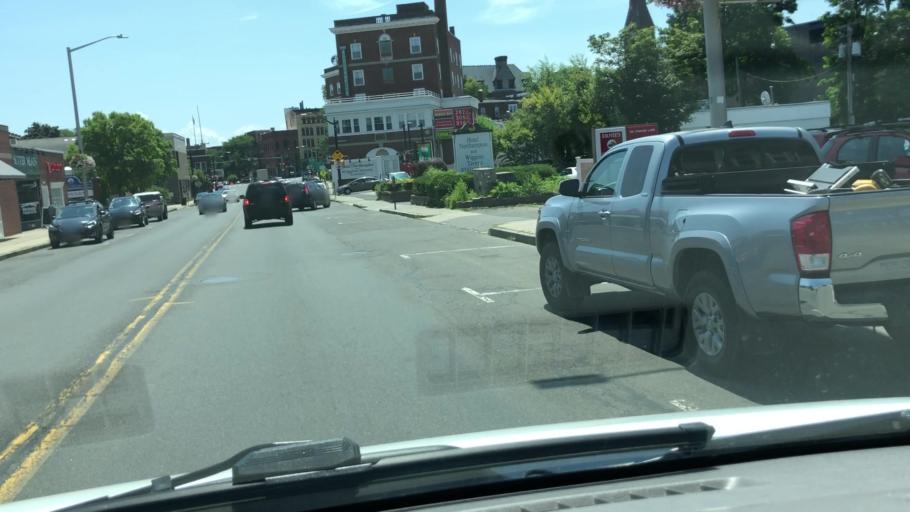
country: US
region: Massachusetts
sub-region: Hampshire County
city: Northampton
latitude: 42.3212
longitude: -72.6315
